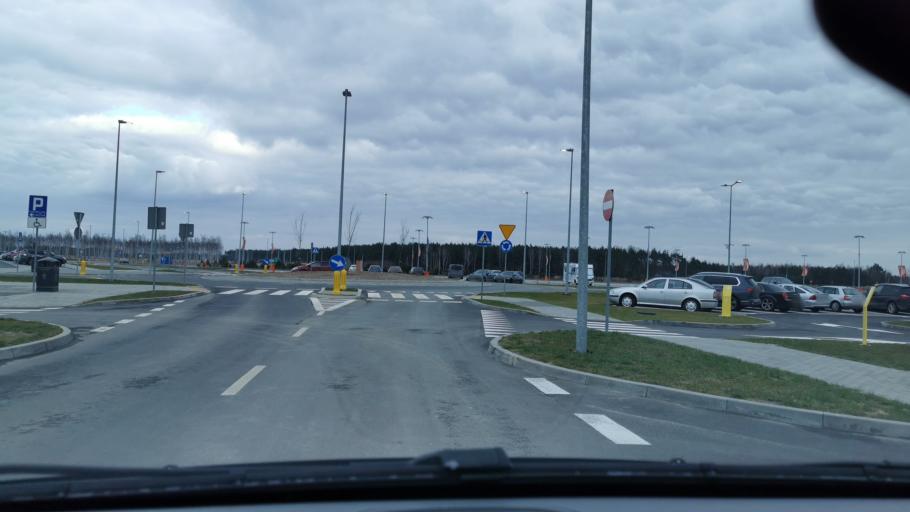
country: PL
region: Masovian Voivodeship
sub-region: Powiat zyrardowski
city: Mszczonow
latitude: 51.9872
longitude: 20.4612
